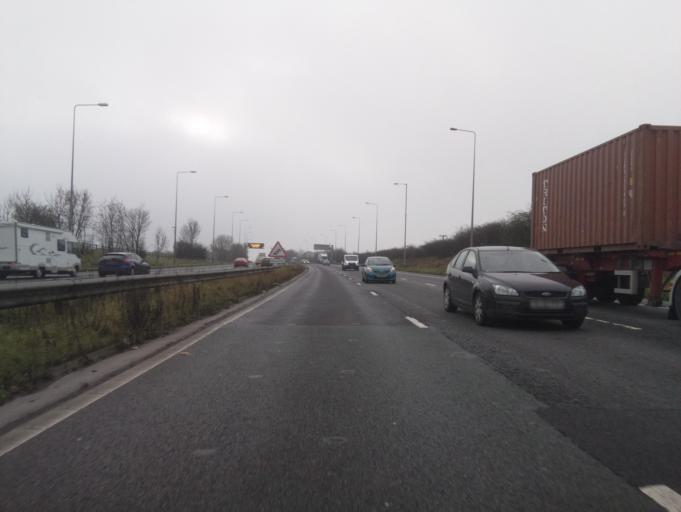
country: GB
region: England
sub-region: Borough of Wigan
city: Shevington
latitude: 53.5554
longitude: -2.7026
